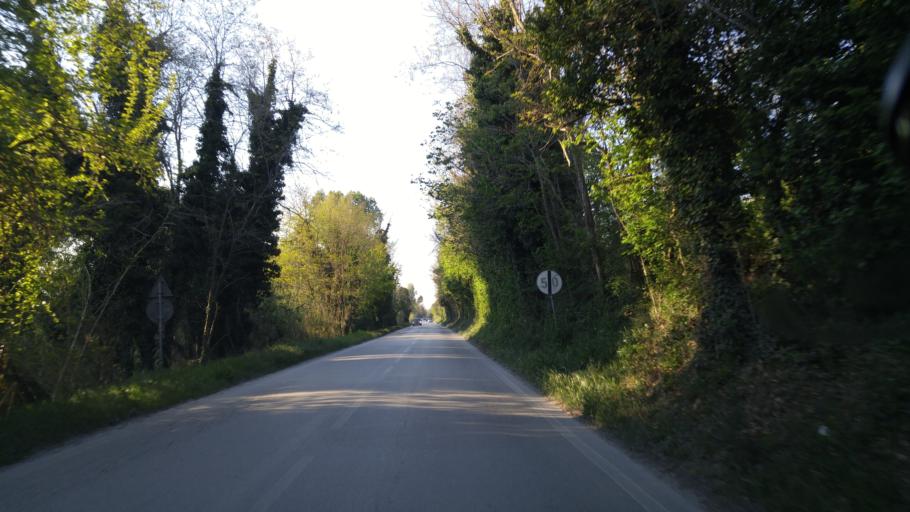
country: IT
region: The Marches
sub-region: Provincia di Pesaro e Urbino
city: Bellocchi
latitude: 43.8042
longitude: 13.0203
